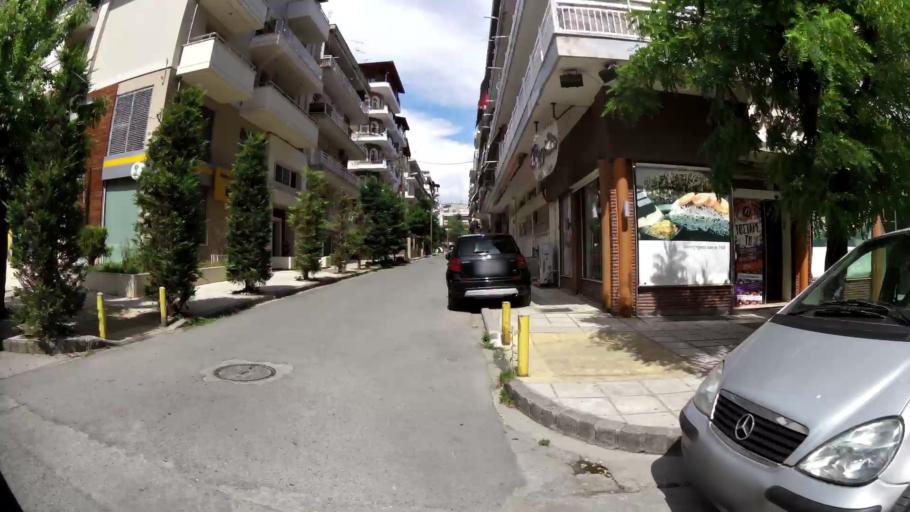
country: GR
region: Central Macedonia
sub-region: Nomos Thessalonikis
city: Triandria
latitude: 40.6079
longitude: 22.9703
